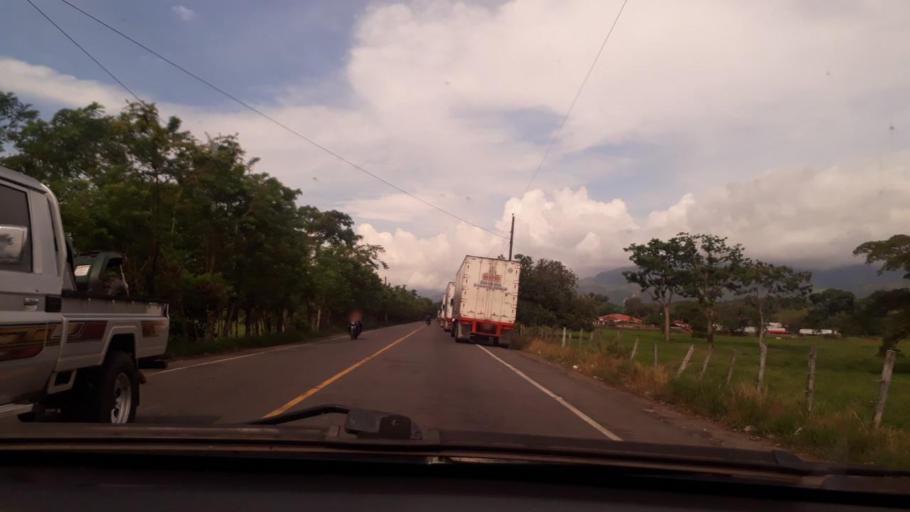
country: HN
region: Cortes
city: Potrerillos
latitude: 15.5970
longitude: -88.3786
